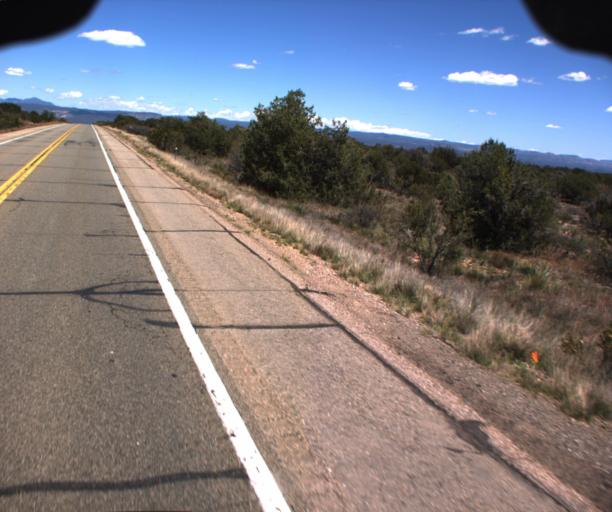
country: US
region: Arizona
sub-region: Yavapai County
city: Paulden
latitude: 34.9360
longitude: -112.4339
